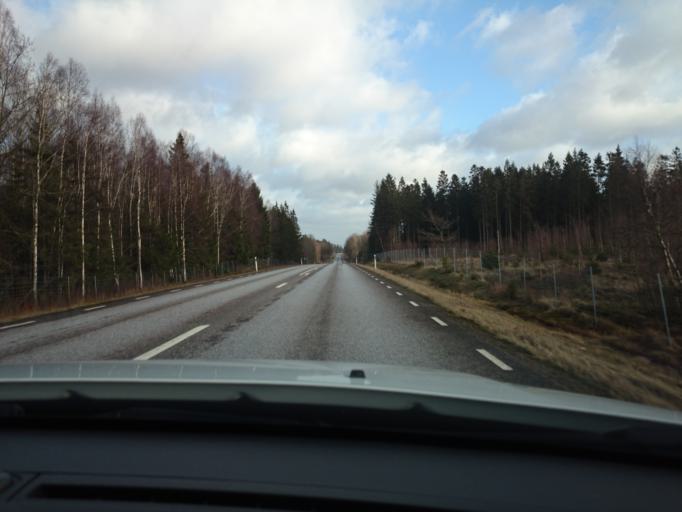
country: SE
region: Halland
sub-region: Hylte Kommun
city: Hyltebruk
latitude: 57.0326
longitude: 13.2793
